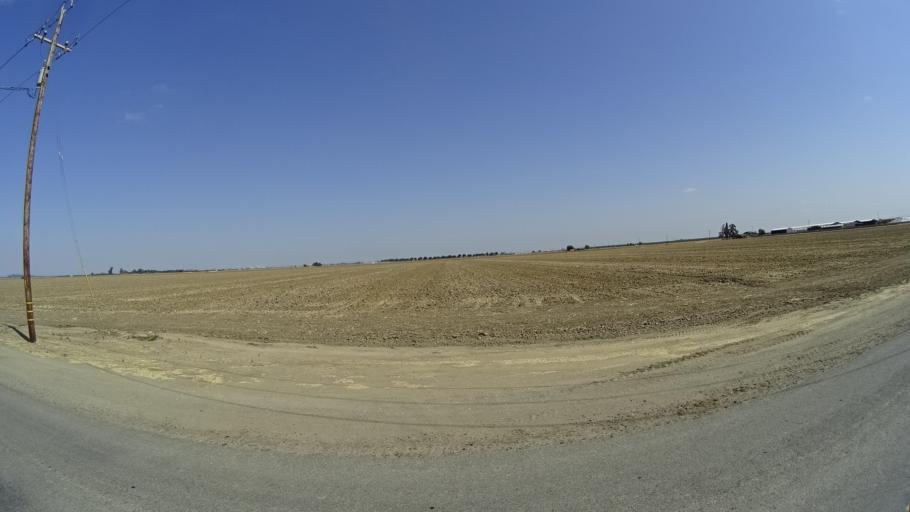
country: US
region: California
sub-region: Kings County
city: Home Garden
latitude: 36.2260
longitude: -119.6222
